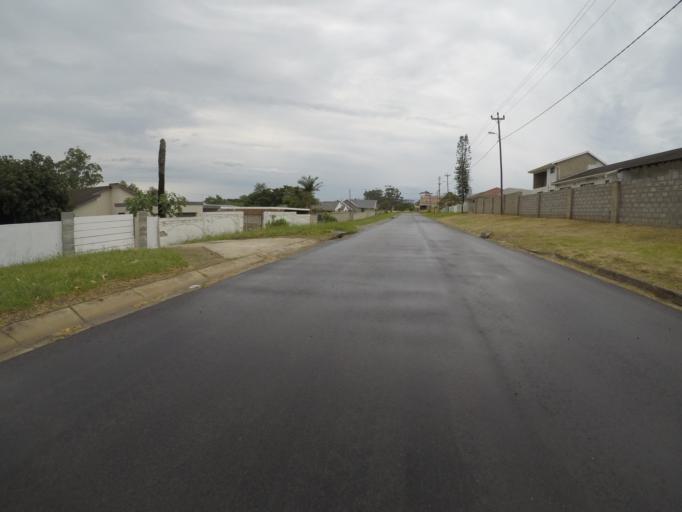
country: ZA
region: Eastern Cape
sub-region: Buffalo City Metropolitan Municipality
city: East London
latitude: -32.9664
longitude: 27.8466
